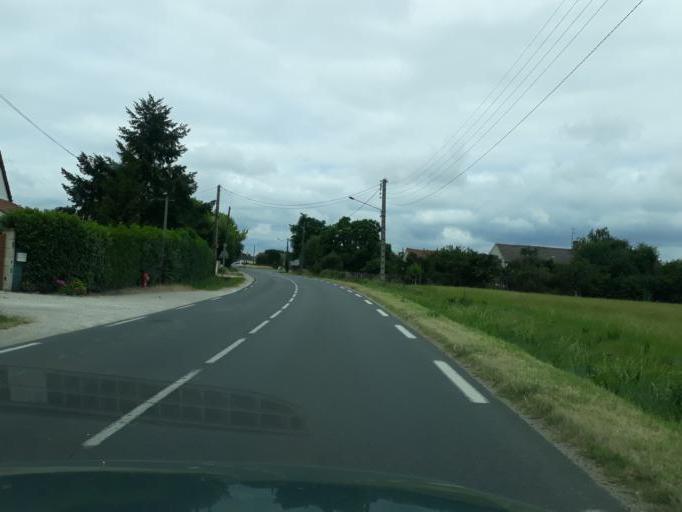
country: FR
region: Centre
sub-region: Departement du Loiret
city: Sandillon
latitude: 47.8521
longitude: 2.0117
